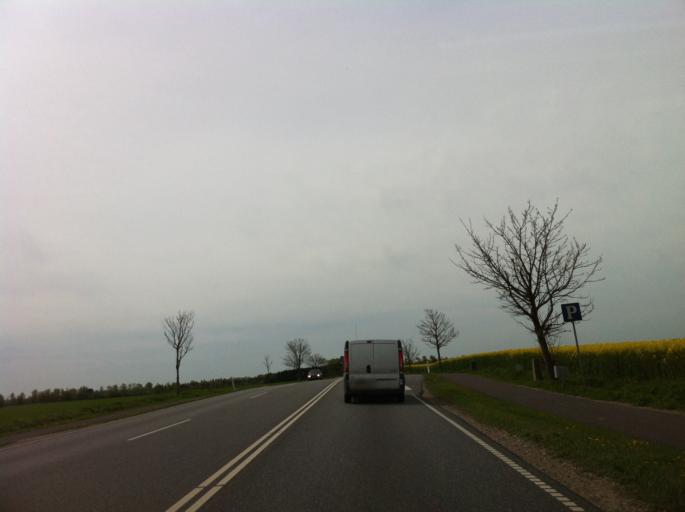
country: DK
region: Zealand
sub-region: Roskilde Kommune
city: Svogerslev
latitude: 55.6090
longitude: 12.0360
